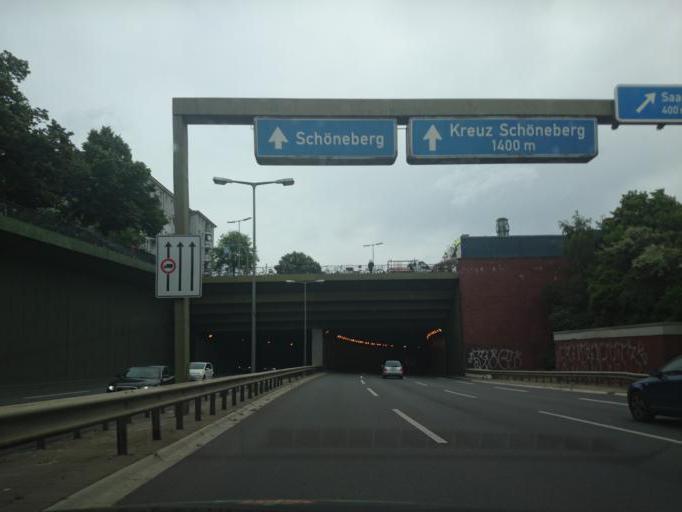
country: DE
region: Berlin
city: Steglitz Bezirk
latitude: 52.4632
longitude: 13.3313
